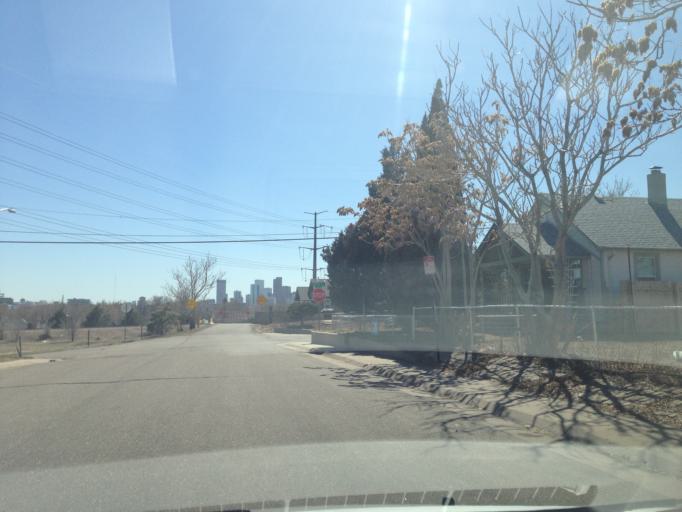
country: US
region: Colorado
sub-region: Adams County
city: Twin Lakes
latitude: 39.7861
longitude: -104.9847
